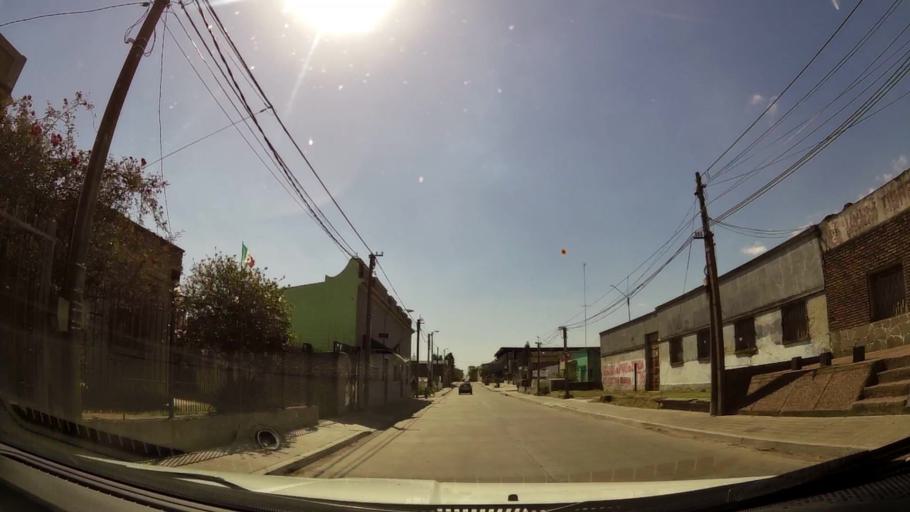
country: UY
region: Montevideo
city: Montevideo
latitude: -34.8475
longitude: -56.2334
